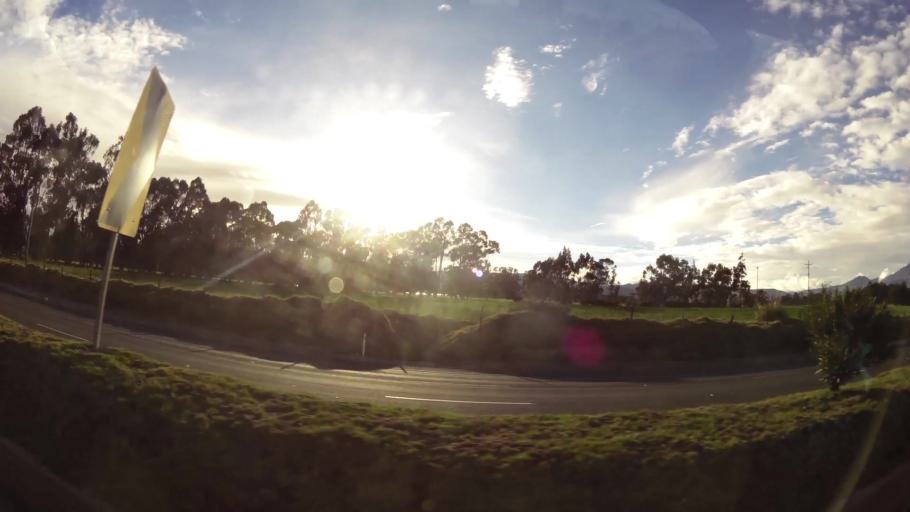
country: EC
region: Cotopaxi
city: Saquisili
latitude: -0.8309
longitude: -78.6189
